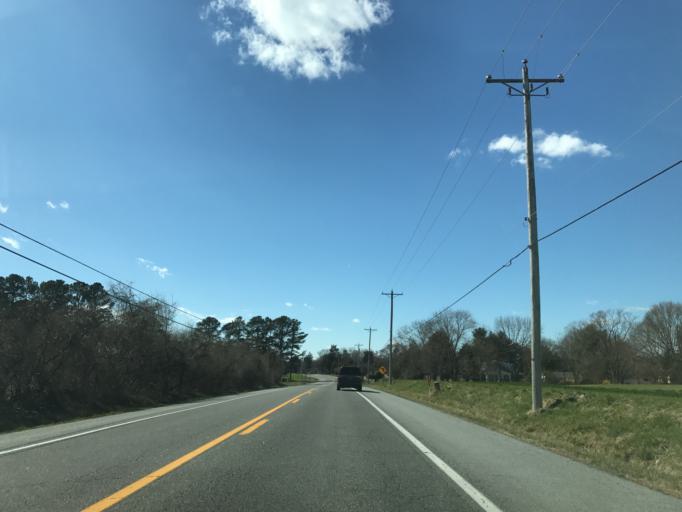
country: US
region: Maryland
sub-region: Kent County
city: Chestertown
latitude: 39.2220
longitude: -76.1606
